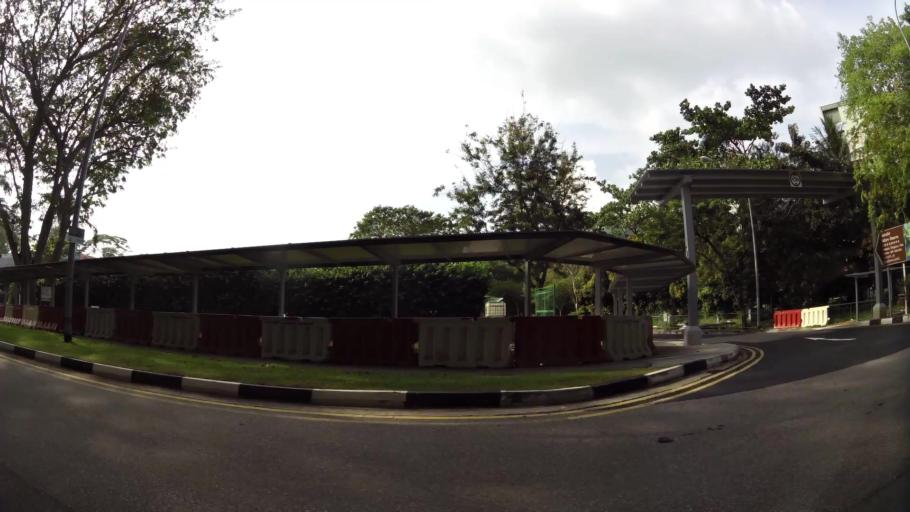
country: SG
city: Singapore
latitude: 1.2724
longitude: 103.8018
